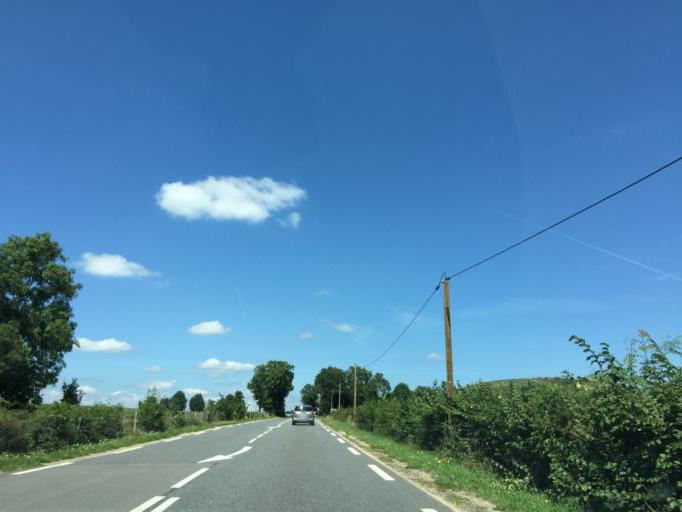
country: FR
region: Midi-Pyrenees
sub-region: Departement de l'Aveyron
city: Laguiole
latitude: 44.6188
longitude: 2.8155
